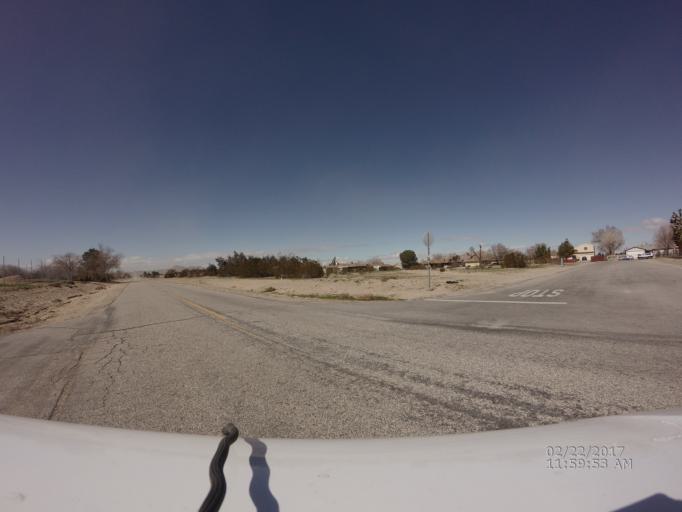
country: US
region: California
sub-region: Los Angeles County
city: Lake Los Angeles
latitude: 34.6238
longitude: -117.8314
